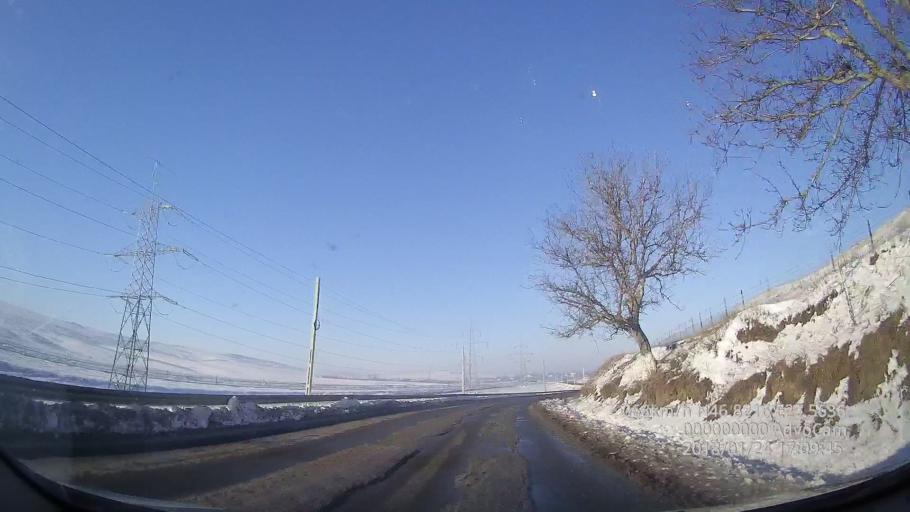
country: RO
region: Vaslui
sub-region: Comuna Vulturesti
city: Vulturesti
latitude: 46.8222
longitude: 27.5635
